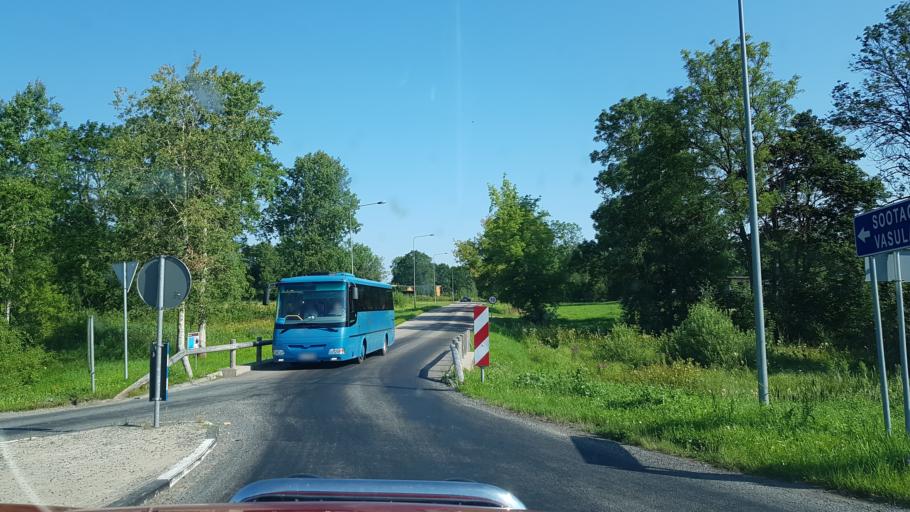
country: EE
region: Tartu
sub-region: Tartu linn
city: Tartu
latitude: 58.4685
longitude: 26.7274
